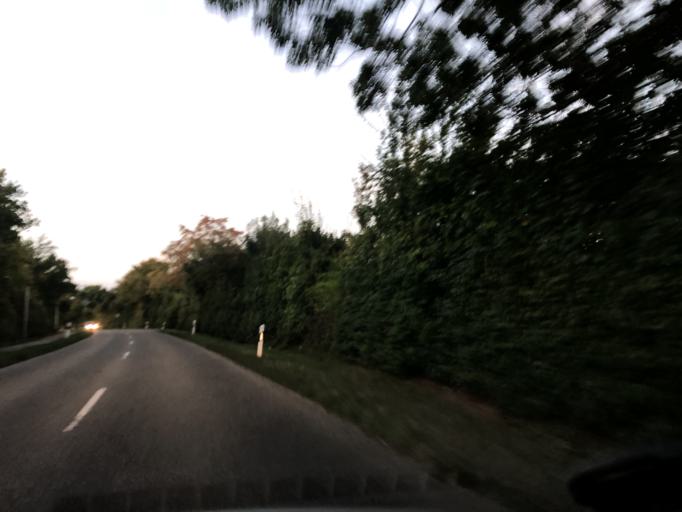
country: DE
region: Baden-Wuerttemberg
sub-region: Regierungsbezirk Stuttgart
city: Erdmannhausen
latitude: 48.8794
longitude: 9.2808
